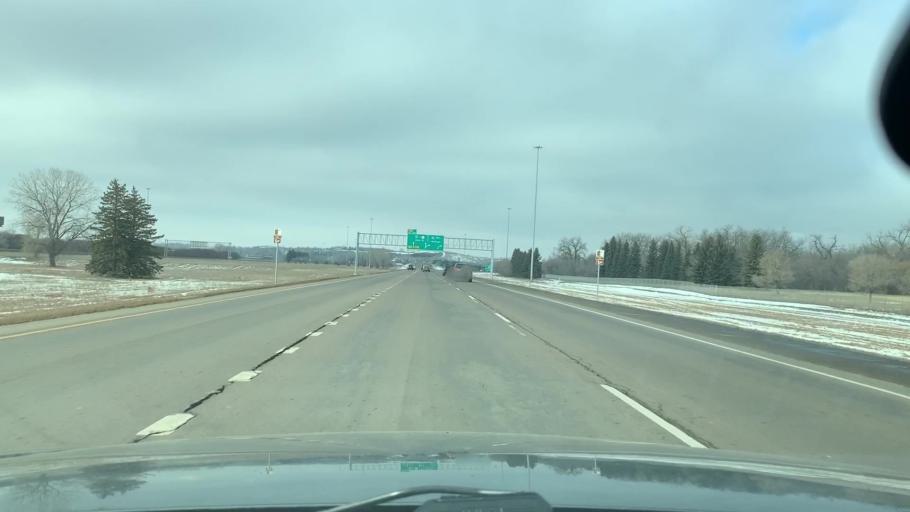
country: US
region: North Dakota
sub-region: Morton County
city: Mandan
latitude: 46.8246
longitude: -100.8480
